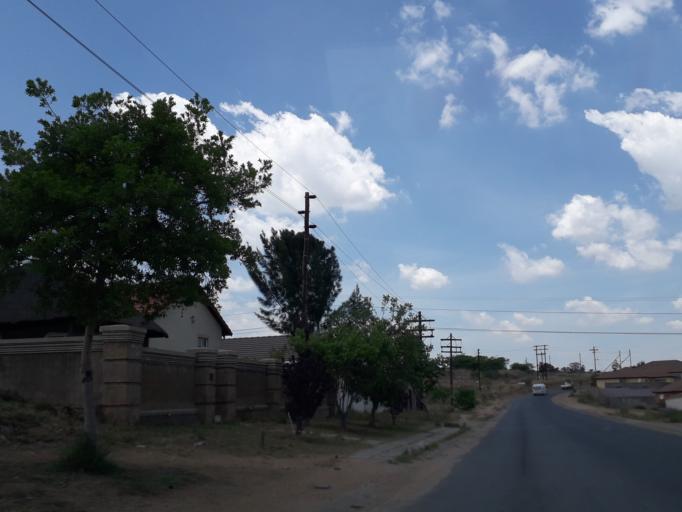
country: ZA
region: Gauteng
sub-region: West Rand District Municipality
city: Muldersdriseloop
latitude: -26.0403
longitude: 27.9230
